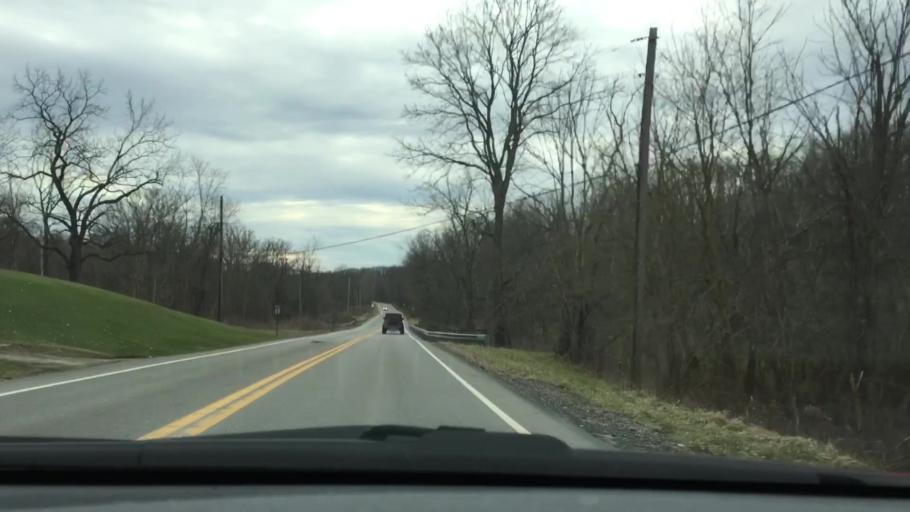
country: US
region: Pennsylvania
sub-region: Washington County
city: McDonald
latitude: 40.3451
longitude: -80.2405
